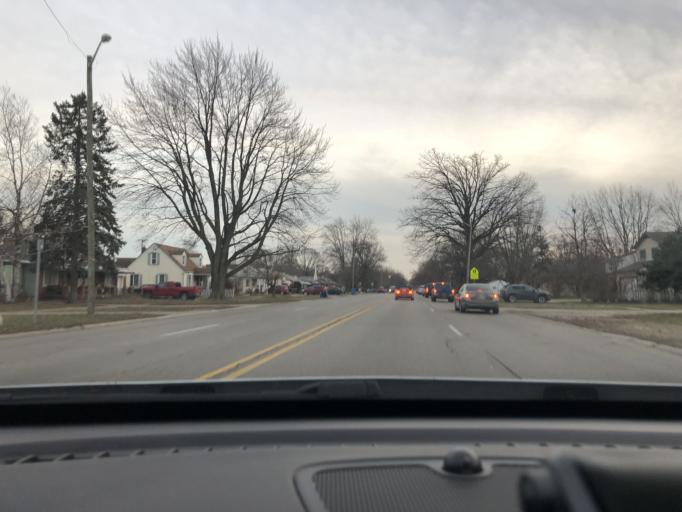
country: US
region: Michigan
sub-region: Wayne County
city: Allen Park
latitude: 42.2788
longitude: -83.2315
